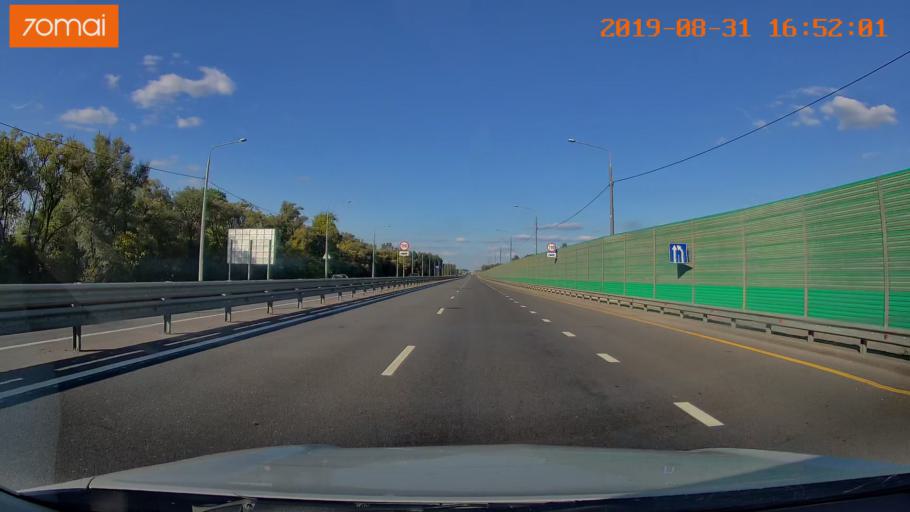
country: RU
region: Kaluga
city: Pyatovskiy
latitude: 54.7353
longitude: 36.1829
